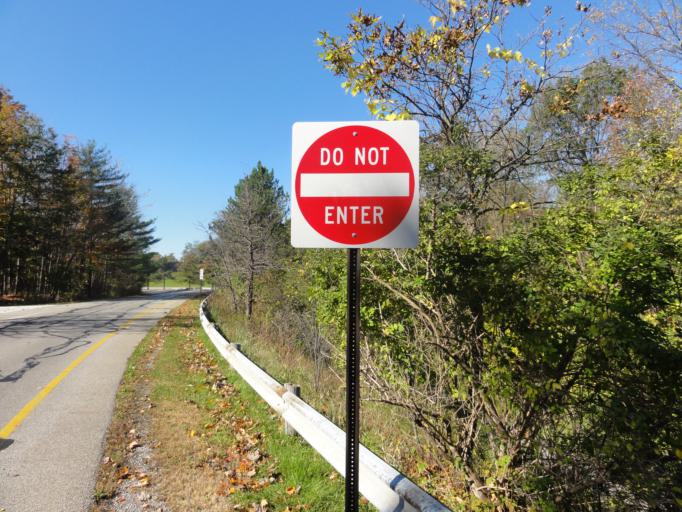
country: US
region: Ohio
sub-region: Cuyahoga County
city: Middleburg Heights
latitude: 41.3598
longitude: -81.8233
